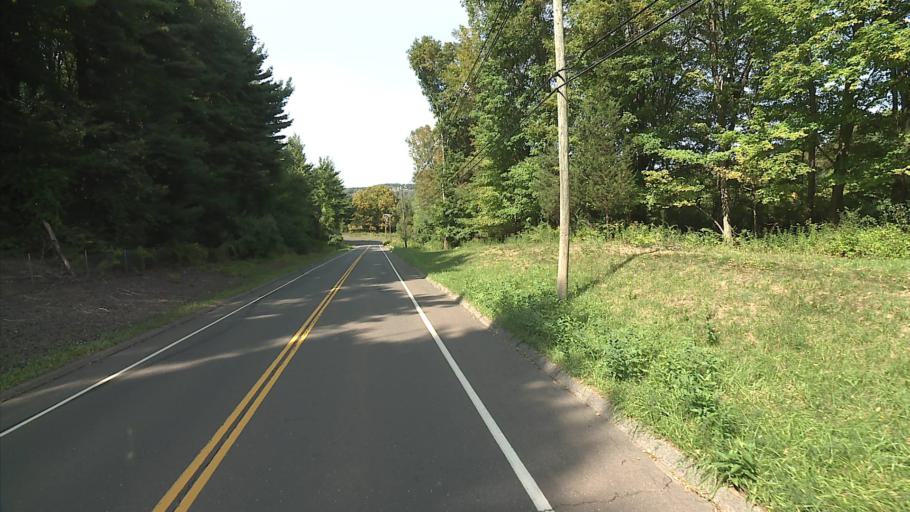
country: US
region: Connecticut
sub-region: Fairfield County
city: Newtown
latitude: 41.4034
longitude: -73.2764
